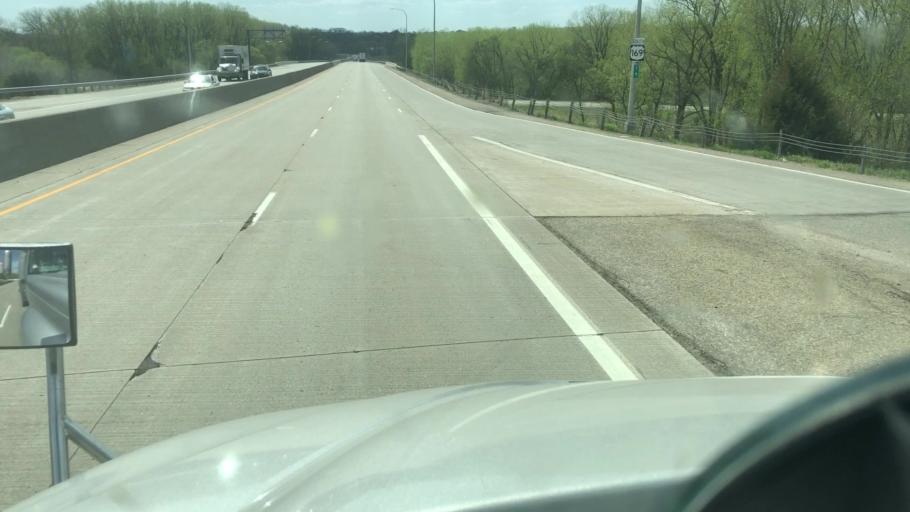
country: US
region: Minnesota
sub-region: Le Sueur County
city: Le Sueur
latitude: 44.4831
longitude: -93.8954
